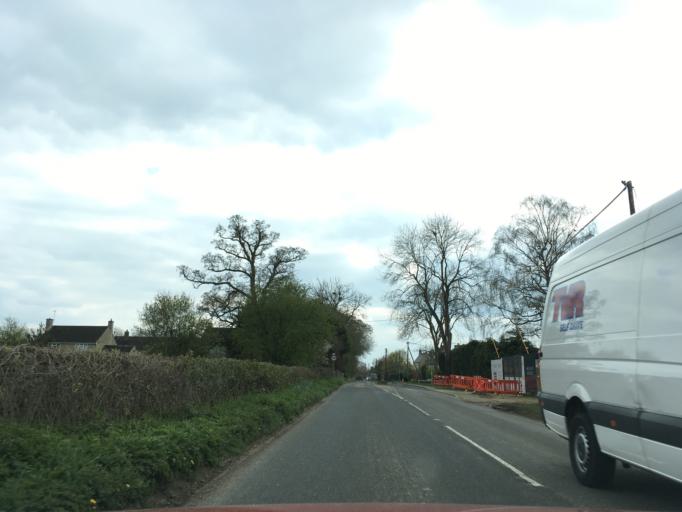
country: GB
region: England
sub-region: Oxfordshire
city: Kidlington
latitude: 51.8798
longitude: -1.2736
